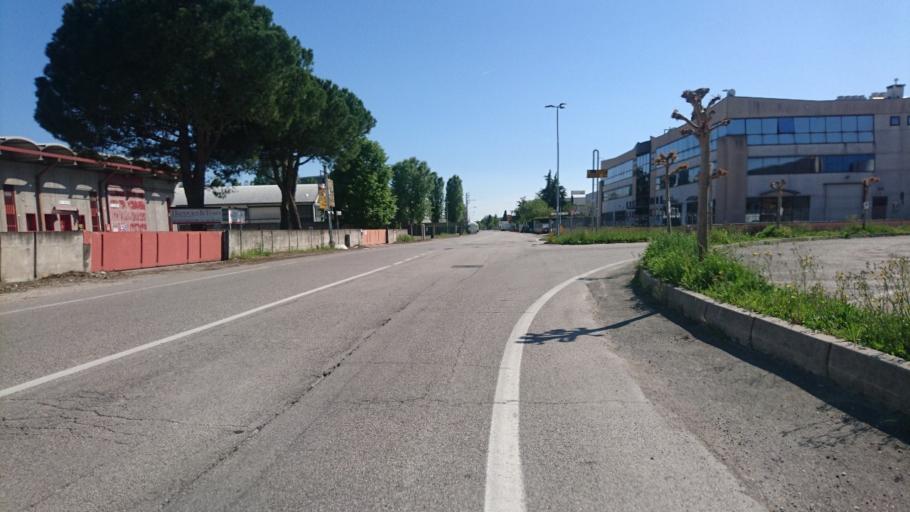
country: IT
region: Veneto
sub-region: Provincia di Venezia
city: Marcon-Gaggio-Colmello
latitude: 45.5488
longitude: 12.2923
